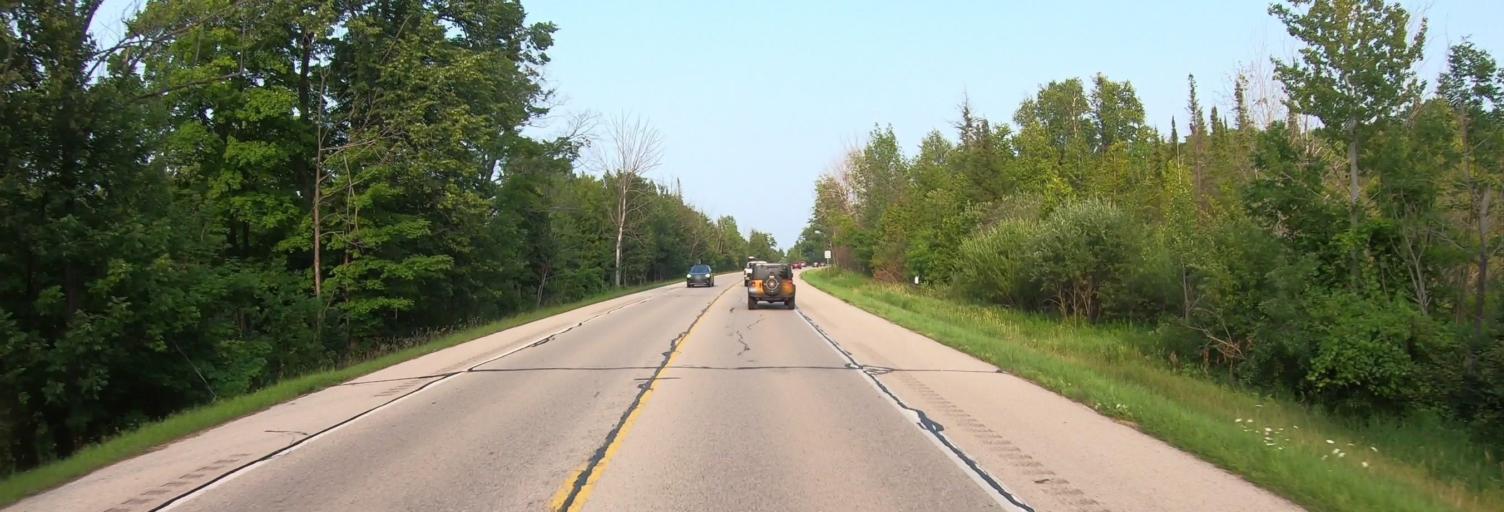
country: US
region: Michigan
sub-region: Charlevoix County
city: Charlevoix
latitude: 45.3697
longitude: -85.1371
